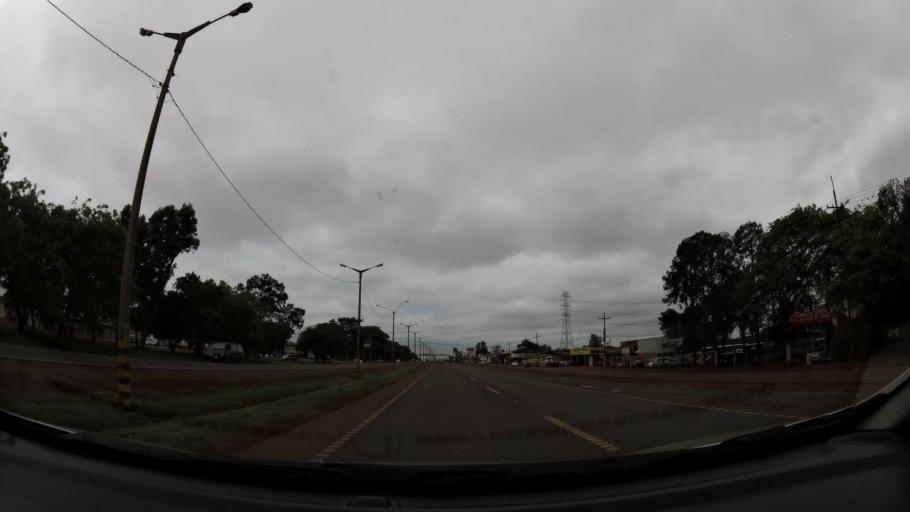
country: PY
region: Alto Parana
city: Ciudad del Este
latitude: -25.4956
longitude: -54.6908
